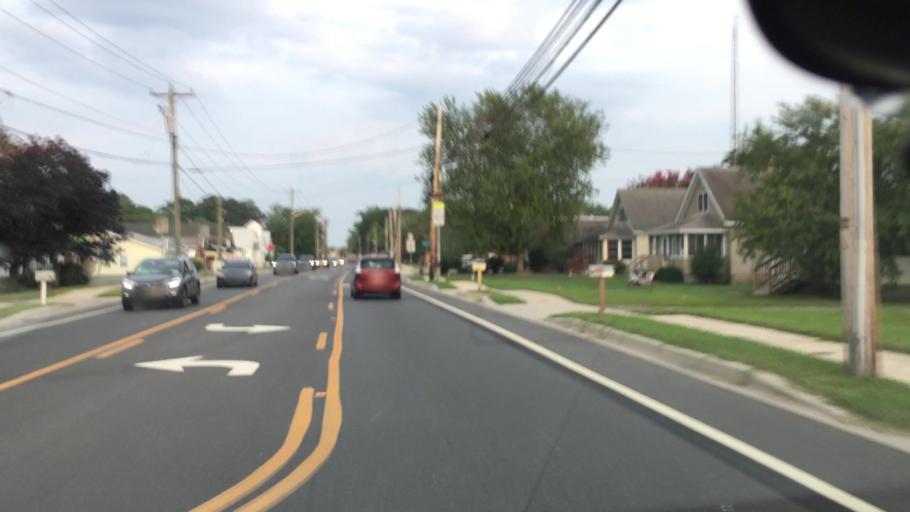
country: US
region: Delaware
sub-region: Sussex County
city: Ocean View
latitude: 38.5461
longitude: -75.1023
